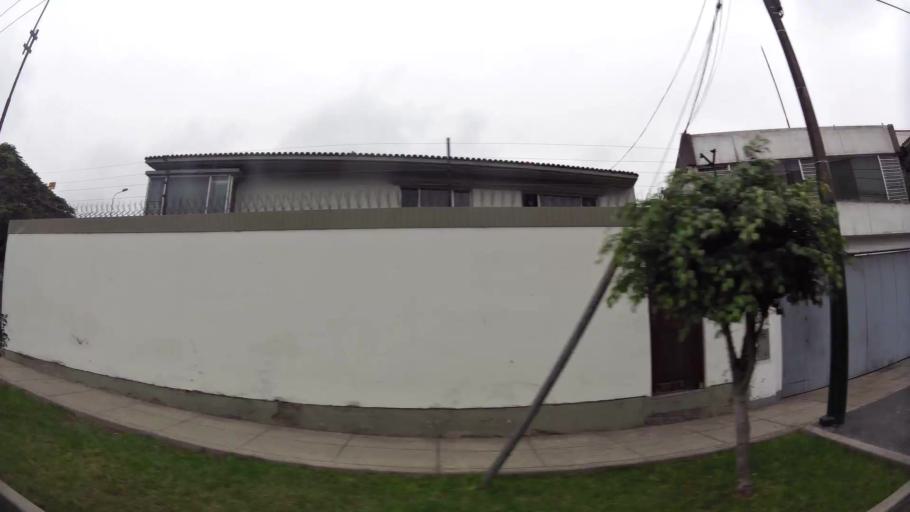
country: PE
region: Lima
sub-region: Lima
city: San Luis
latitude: -12.0898
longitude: -77.0088
